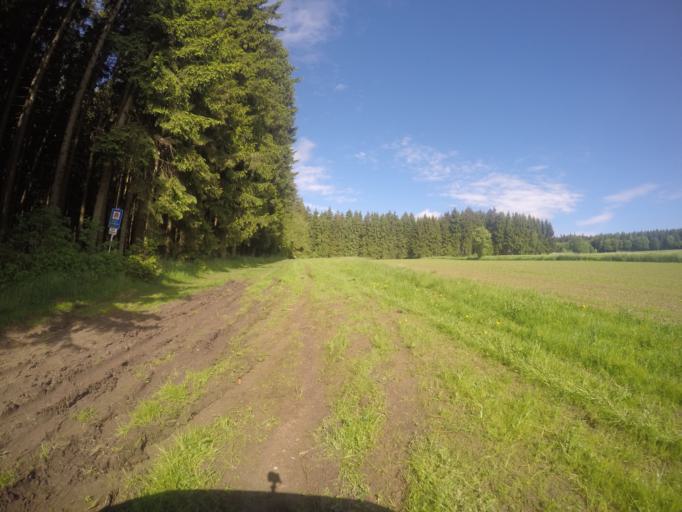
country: DE
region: Bavaria
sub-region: Upper Franconia
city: Schonwald
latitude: 50.1945
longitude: 12.0721
